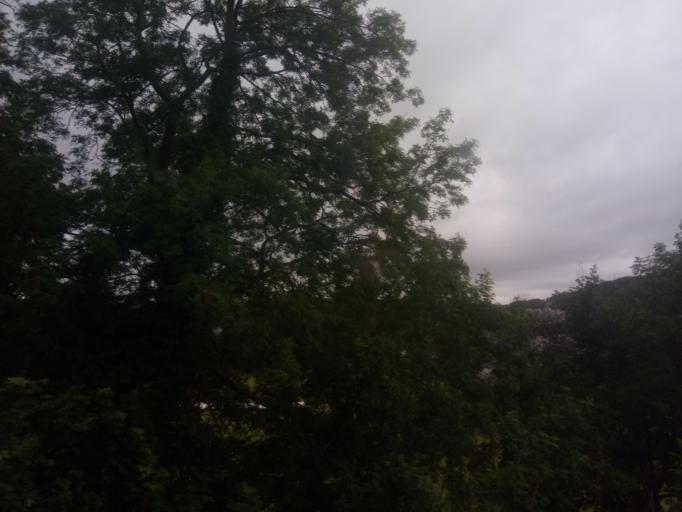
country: GB
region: England
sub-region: North Yorkshire
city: Settle
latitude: 54.0694
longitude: -2.2793
